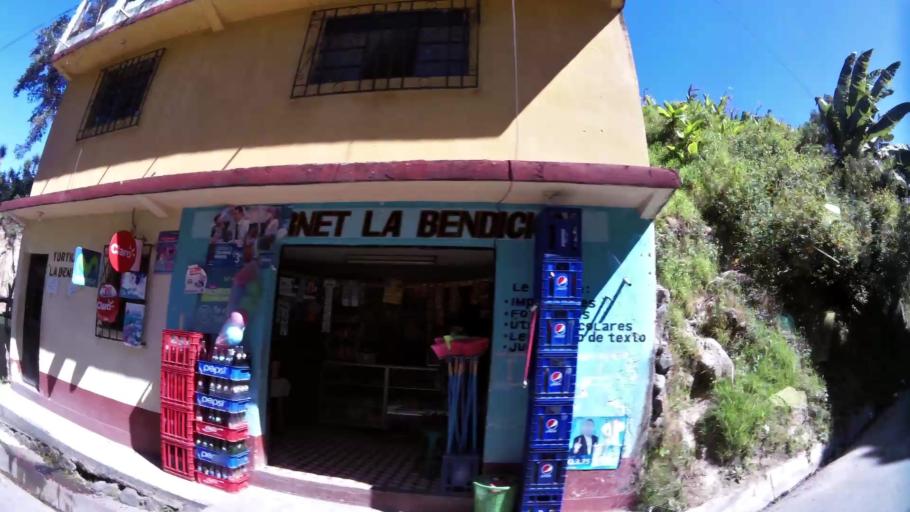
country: GT
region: Solola
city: Solola
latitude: 14.7724
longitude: -91.1803
